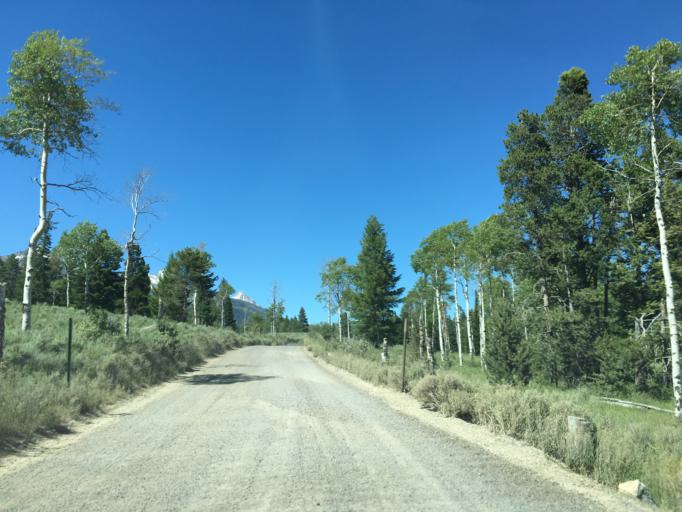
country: US
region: Wyoming
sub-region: Teton County
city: Moose Wilson Road
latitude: 43.6092
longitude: -110.7922
